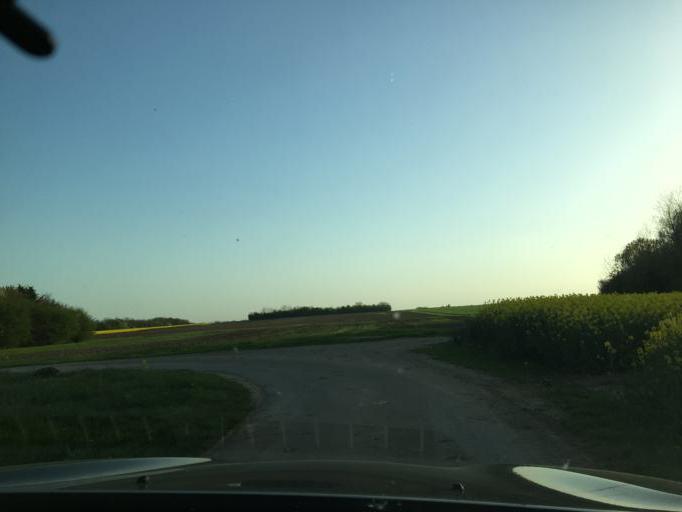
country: FR
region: Centre
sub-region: Departement du Loir-et-Cher
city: Ouzouer-le-Marche
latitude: 47.8299
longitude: 1.5223
